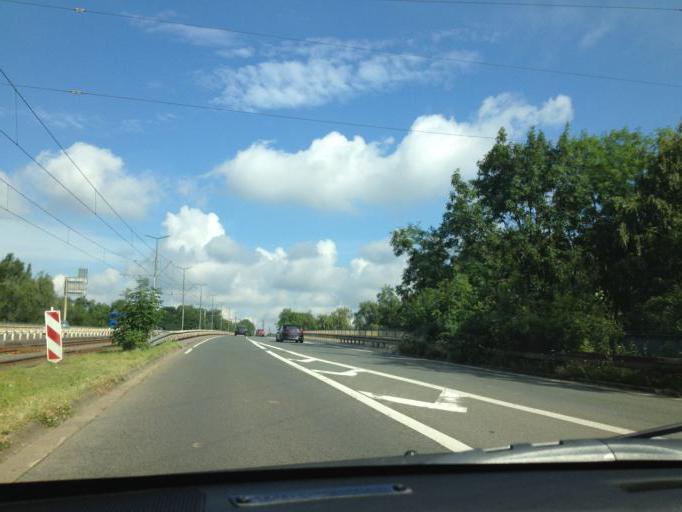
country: DE
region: North Rhine-Westphalia
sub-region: Regierungsbezirk Arnsberg
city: Bochum
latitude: 51.4654
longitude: 7.2754
